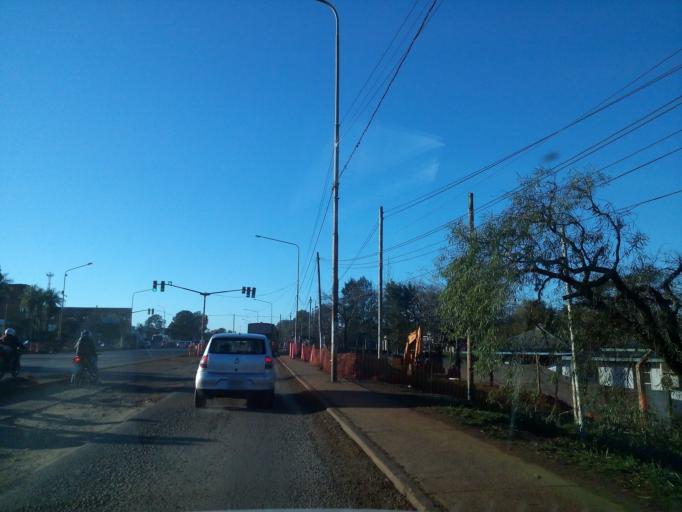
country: AR
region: Misiones
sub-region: Departamento de Capital
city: Posadas
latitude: -27.4337
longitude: -55.8875
